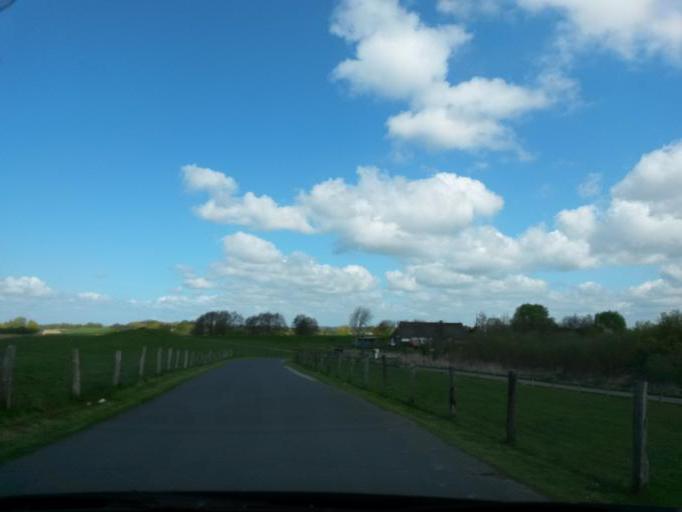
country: DE
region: Schleswig-Holstein
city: Haseldorf
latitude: 53.6363
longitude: 9.5727
